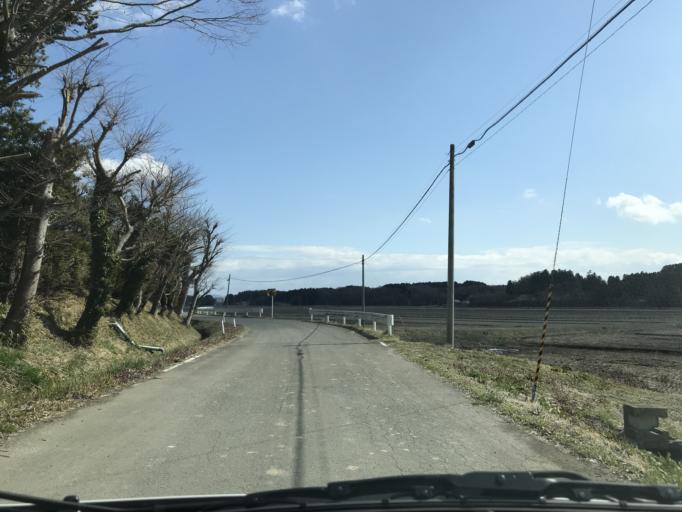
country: JP
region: Miyagi
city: Wakuya
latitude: 38.6792
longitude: 141.1311
